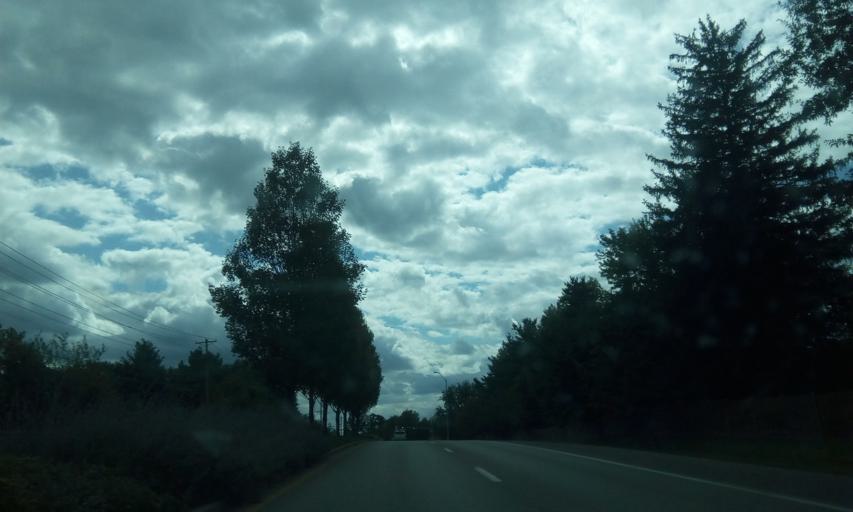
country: US
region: Missouri
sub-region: Saint Louis County
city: Clarkson Valley
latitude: 38.6304
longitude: -90.5768
